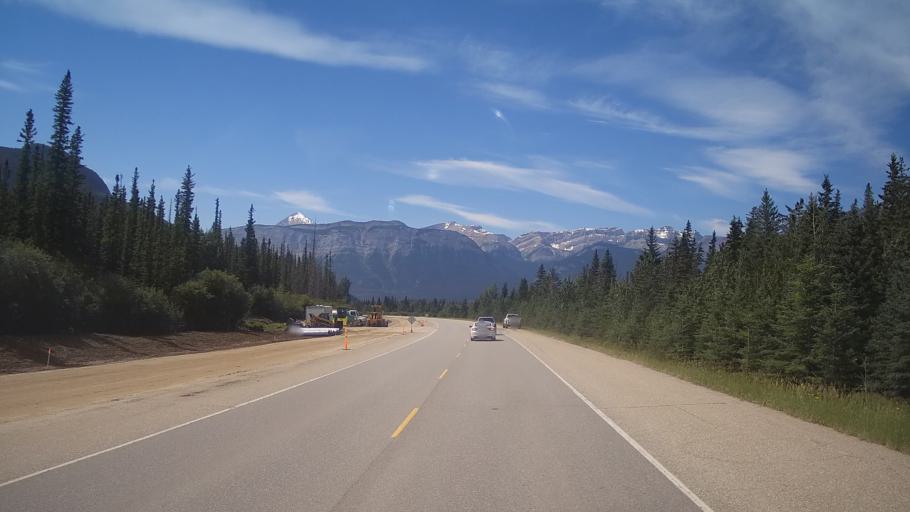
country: CA
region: Alberta
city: Jasper Park Lodge
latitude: 53.0672
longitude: -118.0611
